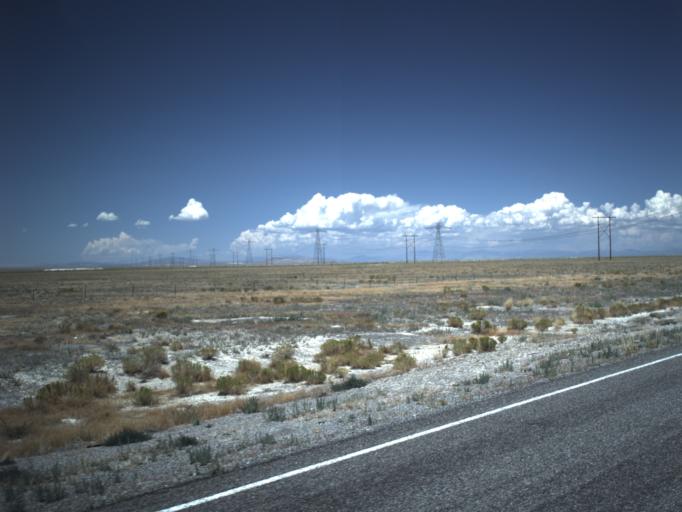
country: US
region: Utah
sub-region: Millard County
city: Delta
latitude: 39.2437
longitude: -112.9089
